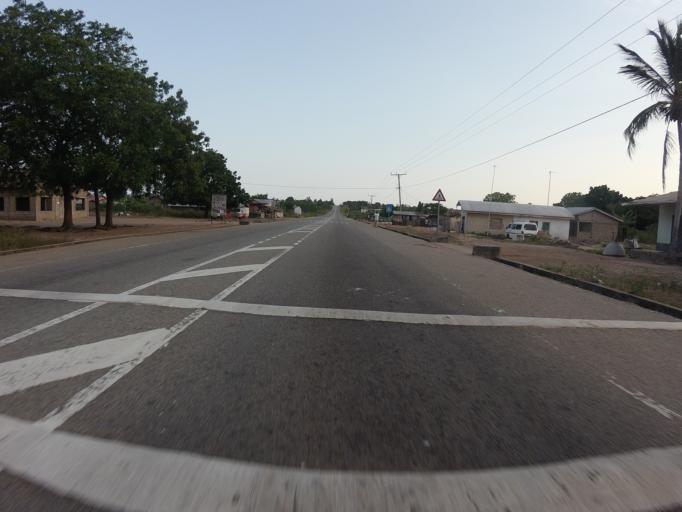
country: GH
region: Volta
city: Anloga
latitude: 6.0587
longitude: 0.6045
